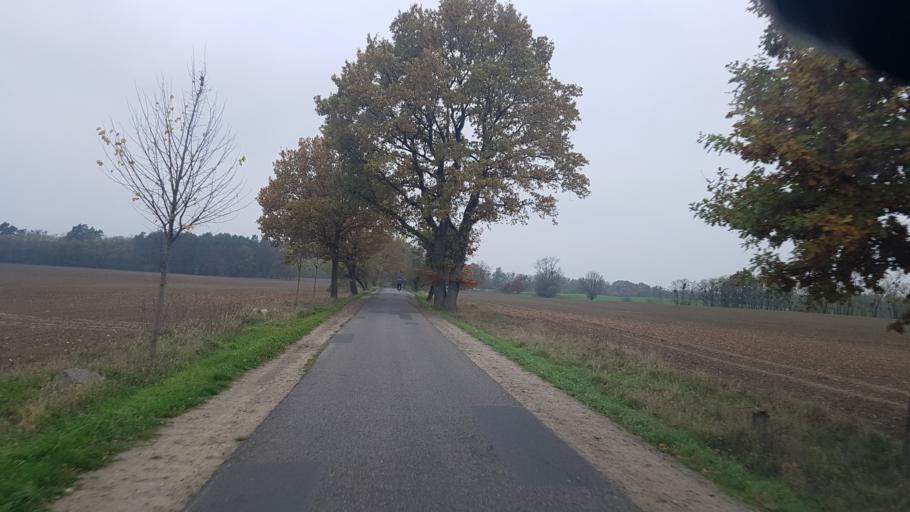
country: DE
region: Brandenburg
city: Lindow
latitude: 52.9430
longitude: 13.0562
